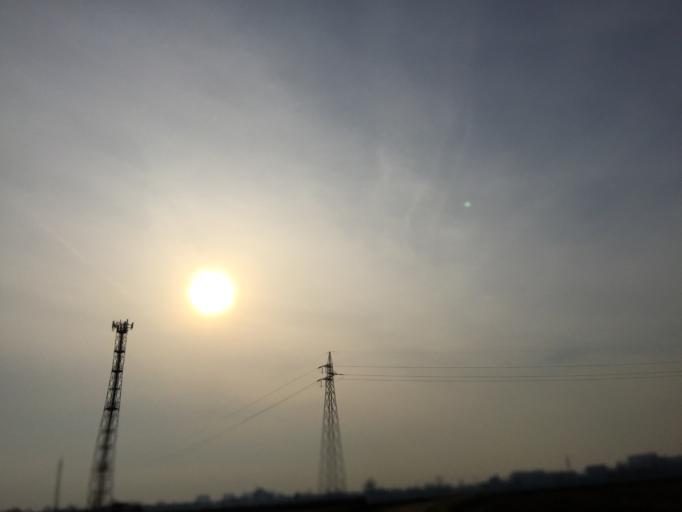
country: IT
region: Lombardy
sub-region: Citta metropolitana di Milano
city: Assago
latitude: 45.4269
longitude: 9.1464
